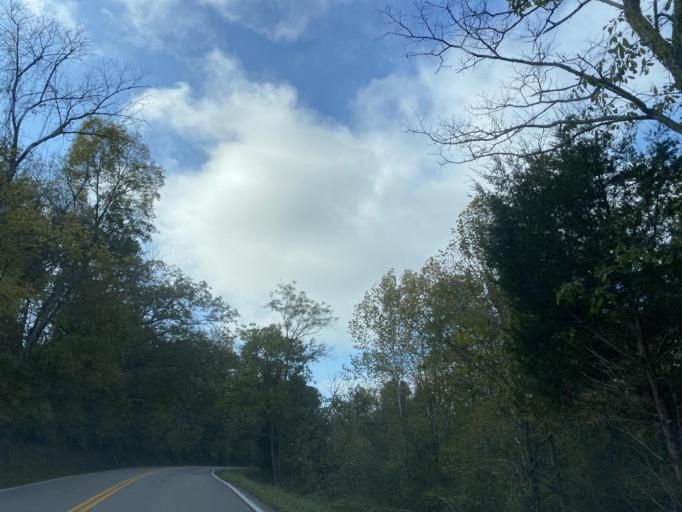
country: US
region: Kentucky
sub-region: Pendleton County
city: Falmouth
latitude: 38.7149
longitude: -84.3016
